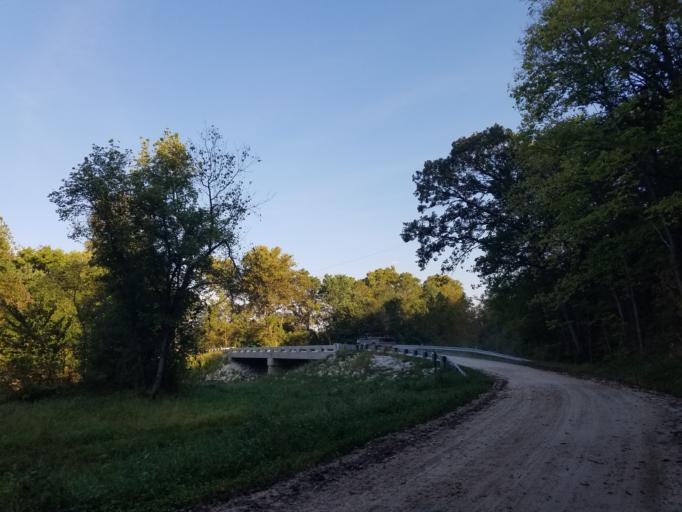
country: US
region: Missouri
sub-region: Cooper County
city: Boonville
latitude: 38.8501
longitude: -92.6574
